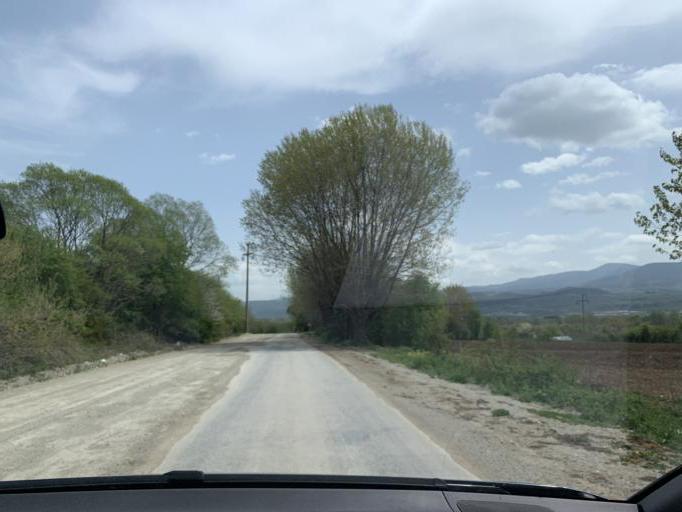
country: TR
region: Bolu
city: Bolu
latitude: 40.7606
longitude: 31.6973
